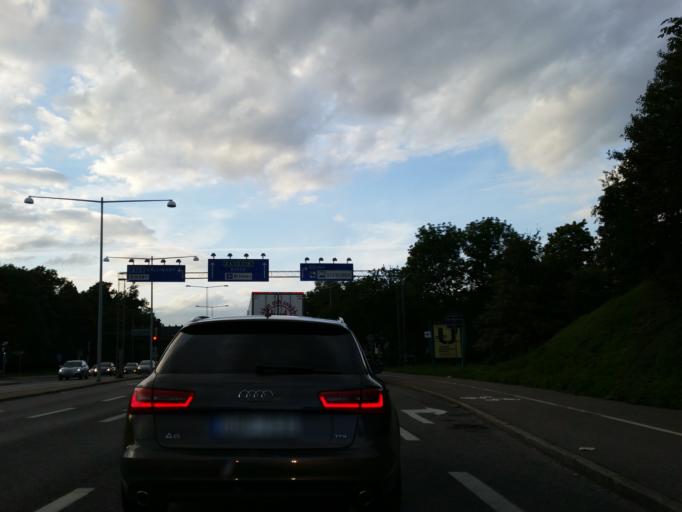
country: SE
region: Stockholm
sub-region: Stockholms Kommun
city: Bromma
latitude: 59.3437
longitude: 17.9601
